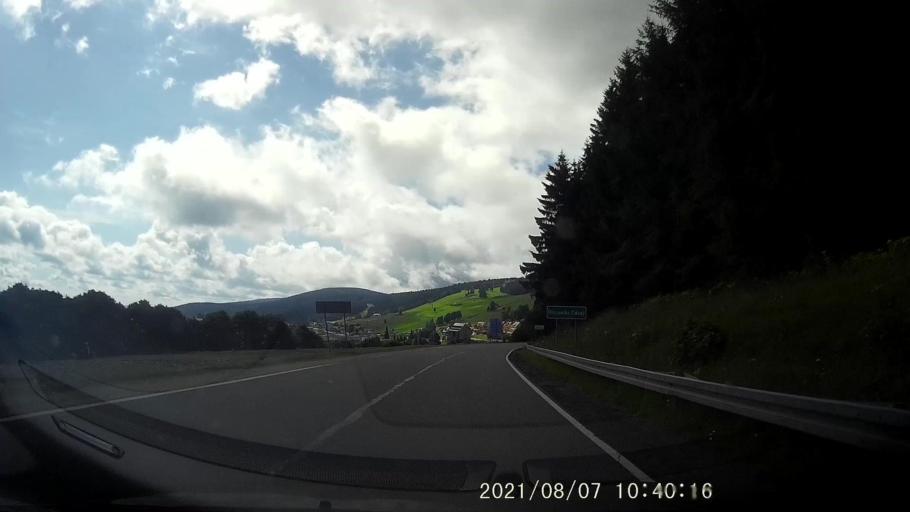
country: PL
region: Lower Silesian Voivodeship
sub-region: Powiat klodzki
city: Duszniki-Zdroj
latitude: 50.3449
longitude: 16.3831
